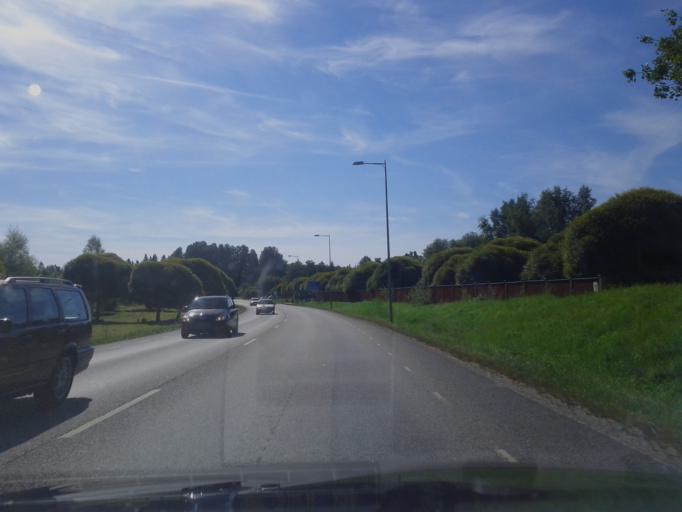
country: SE
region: Stockholm
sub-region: Taby Kommun
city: Taby
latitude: 59.4697
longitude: 18.0524
